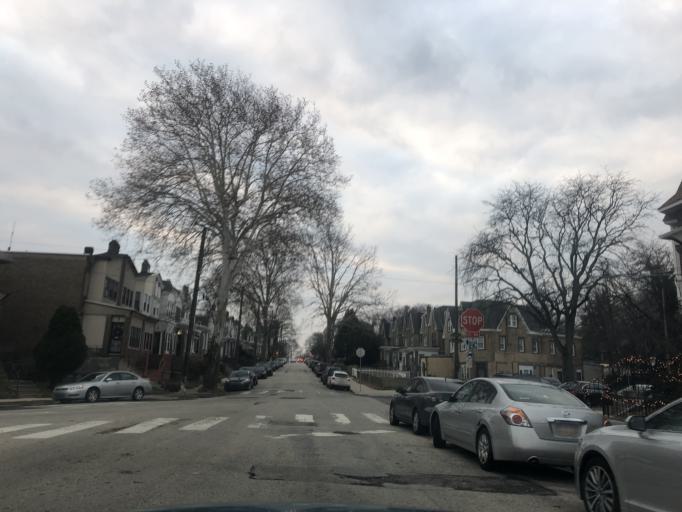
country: US
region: Pennsylvania
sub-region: Delaware County
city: Millbourne
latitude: 39.9832
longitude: -75.2432
